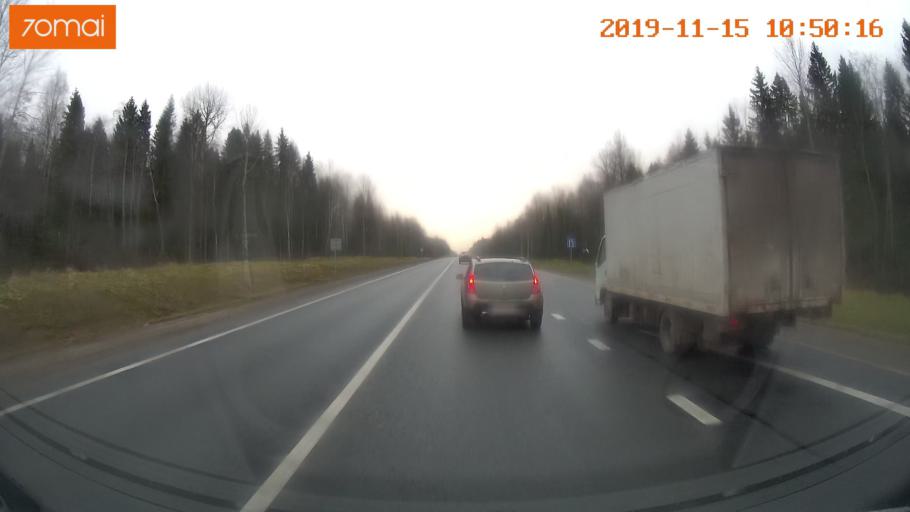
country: RU
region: Vologda
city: Chebsara
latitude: 59.1861
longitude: 38.6778
